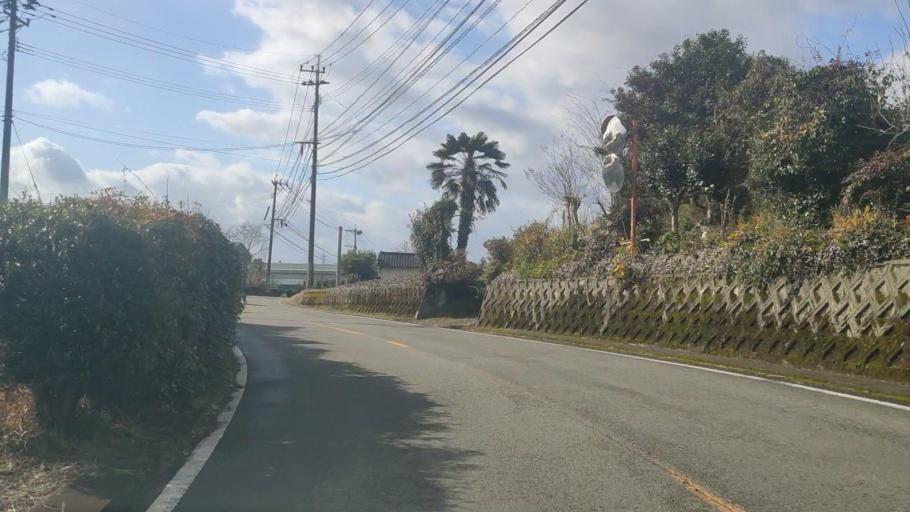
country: JP
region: Kumamoto
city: Hitoyoshi
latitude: 32.2313
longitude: 130.7855
